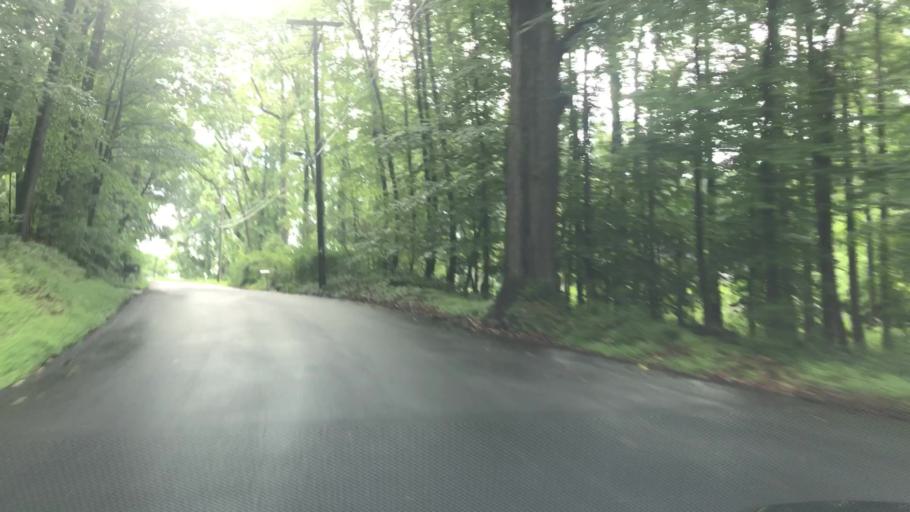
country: US
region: New Jersey
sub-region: Hunterdon County
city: Lebanon
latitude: 40.6697
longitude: -74.8349
